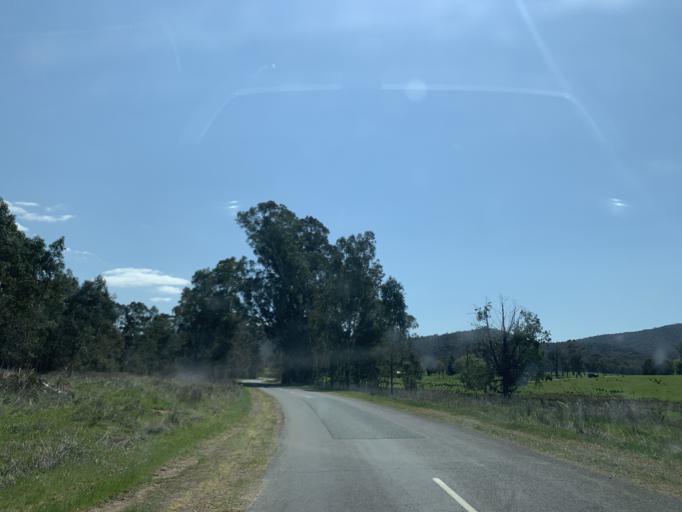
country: AU
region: Victoria
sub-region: Mansfield
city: Mansfield
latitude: -36.7902
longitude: 146.1388
